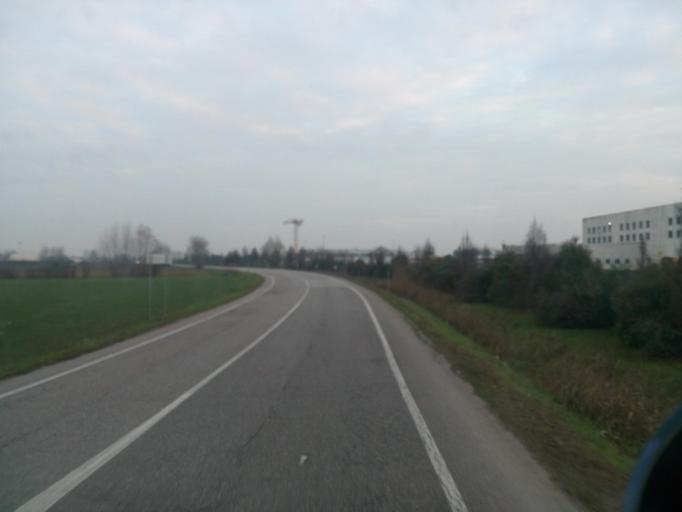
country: IT
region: Veneto
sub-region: Provincia di Verona
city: Pradelle
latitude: 45.2817
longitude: 10.8606
